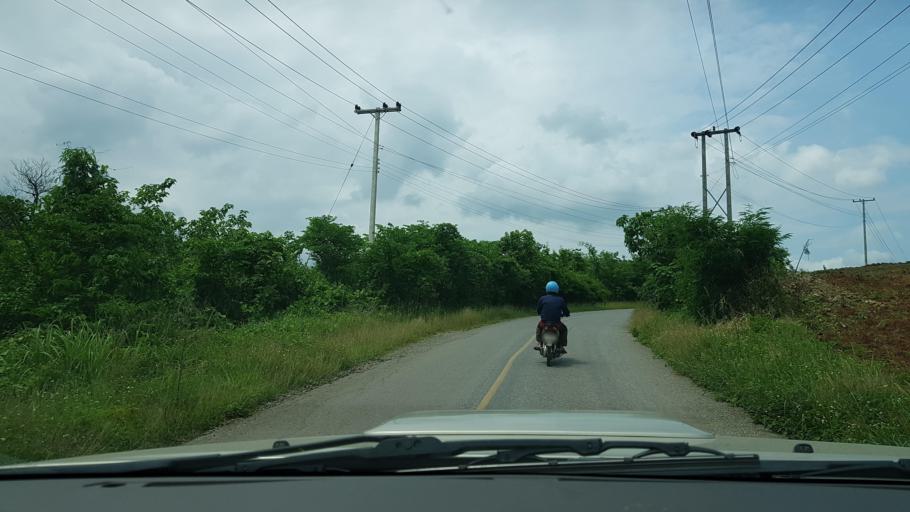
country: TH
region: Nan
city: Chaloem Phra Kiat
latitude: 20.0144
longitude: 101.3183
